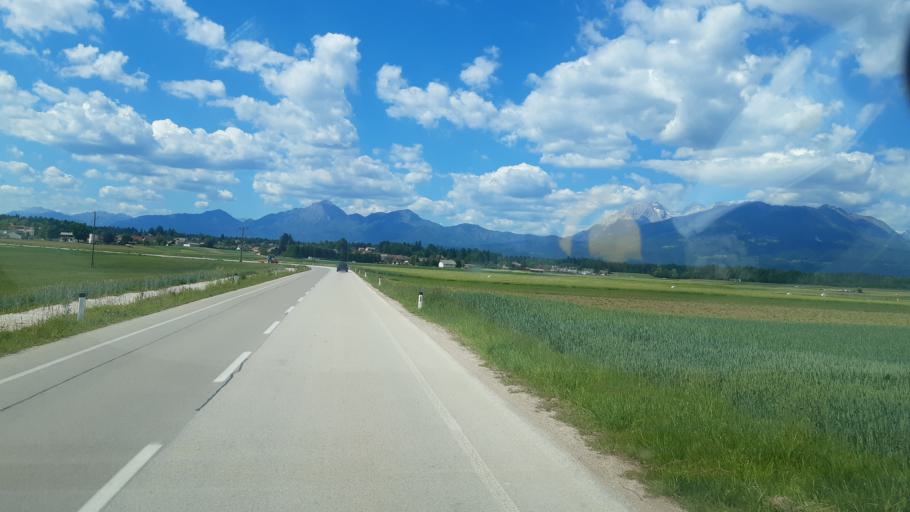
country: SI
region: Vodice
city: Vodice
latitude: 46.1799
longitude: 14.5030
